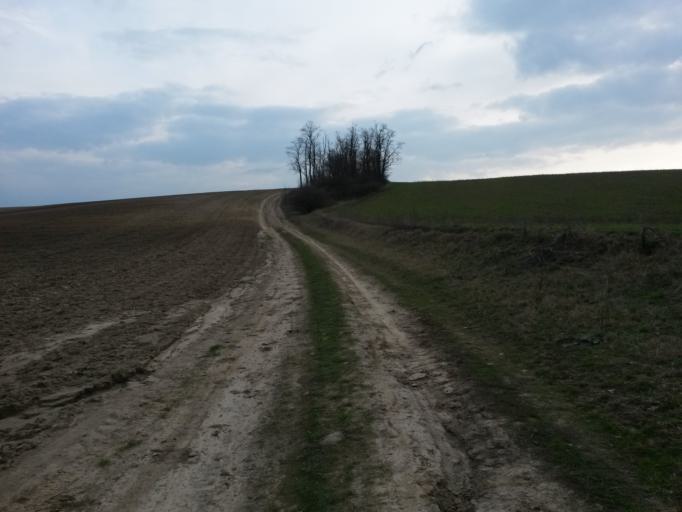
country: HU
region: Pest
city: Perbal
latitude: 47.6213
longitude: 18.7420
